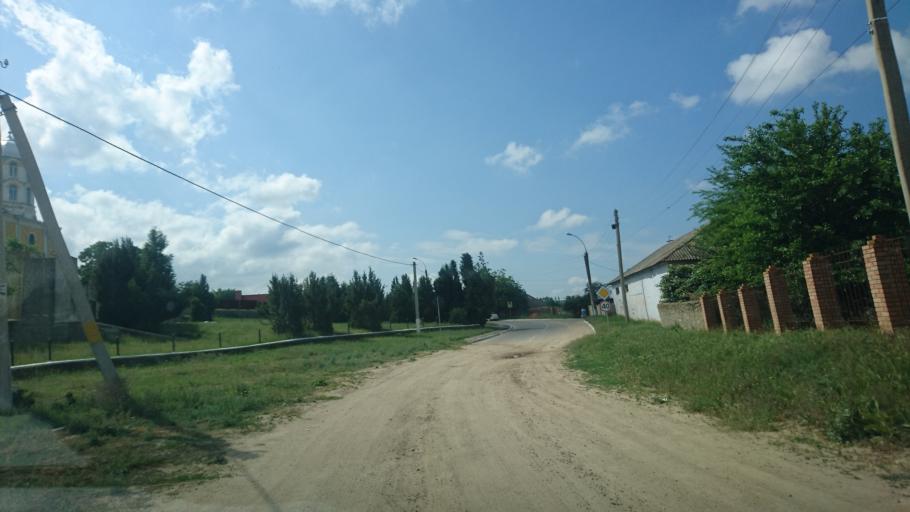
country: MD
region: Telenesti
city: Cocieri
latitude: 47.3571
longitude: 29.1061
